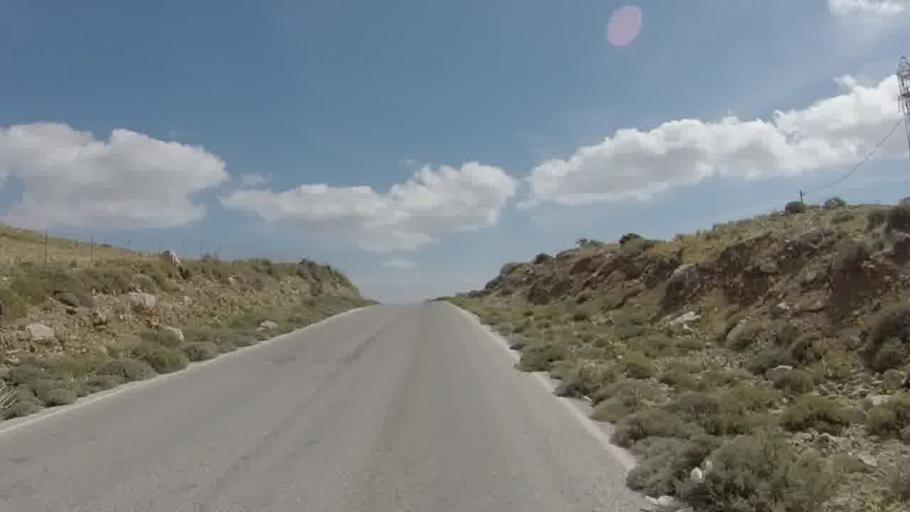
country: GR
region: Crete
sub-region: Nomos Rethymnis
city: Agia Galini
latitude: 35.1580
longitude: 24.6138
